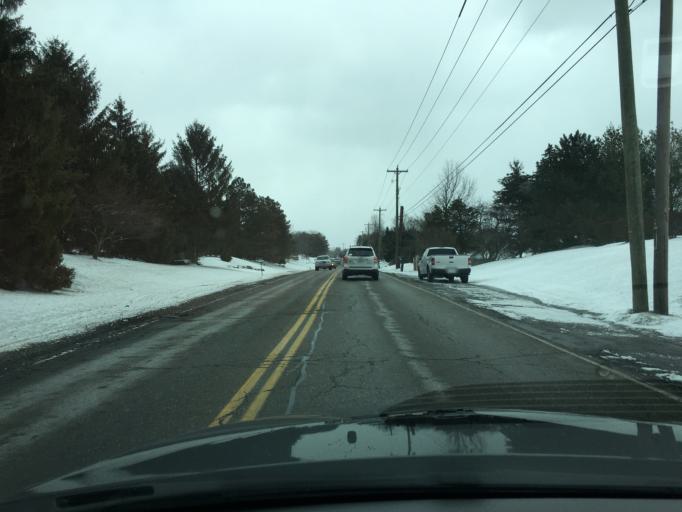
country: US
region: Ohio
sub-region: Summit County
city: Fairlawn
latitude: 41.1404
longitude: -81.5861
